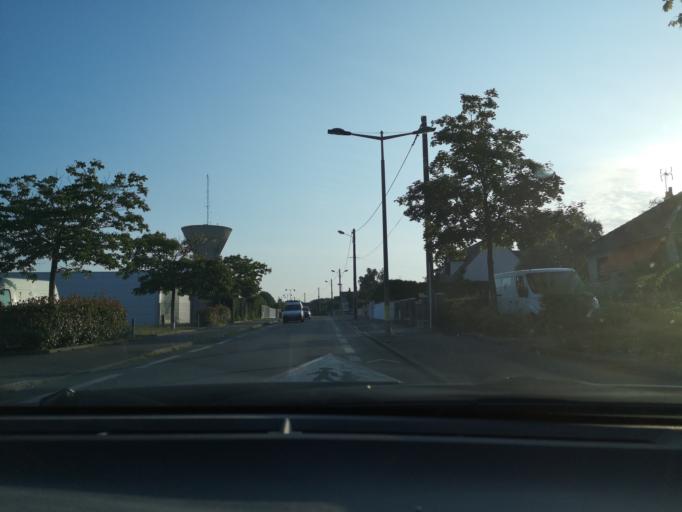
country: FR
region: Centre
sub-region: Departement du Loiret
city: Fleury-les-Aubrais
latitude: 47.9287
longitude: 1.9260
